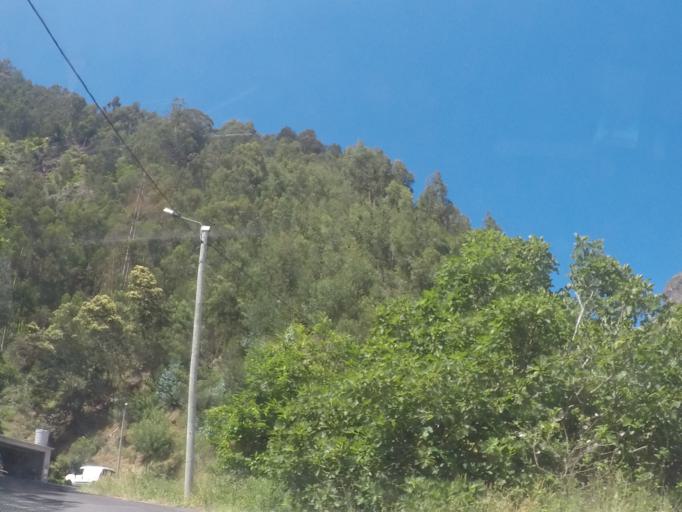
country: PT
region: Madeira
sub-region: Camara de Lobos
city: Curral das Freiras
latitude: 32.7175
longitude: -16.9745
